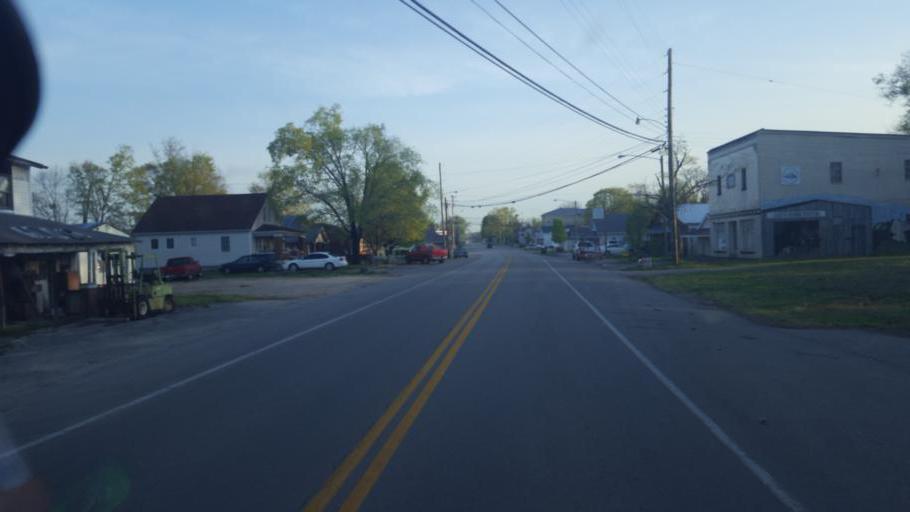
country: US
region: Kentucky
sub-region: Hart County
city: Munfordville
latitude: 37.3752
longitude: -85.9027
